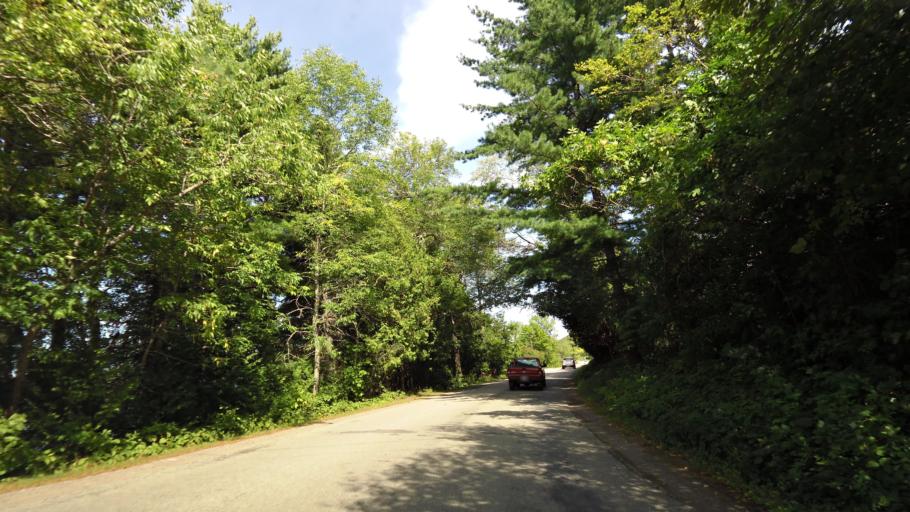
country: CA
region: New Brunswick
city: Hampton
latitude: 45.6096
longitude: -65.9050
